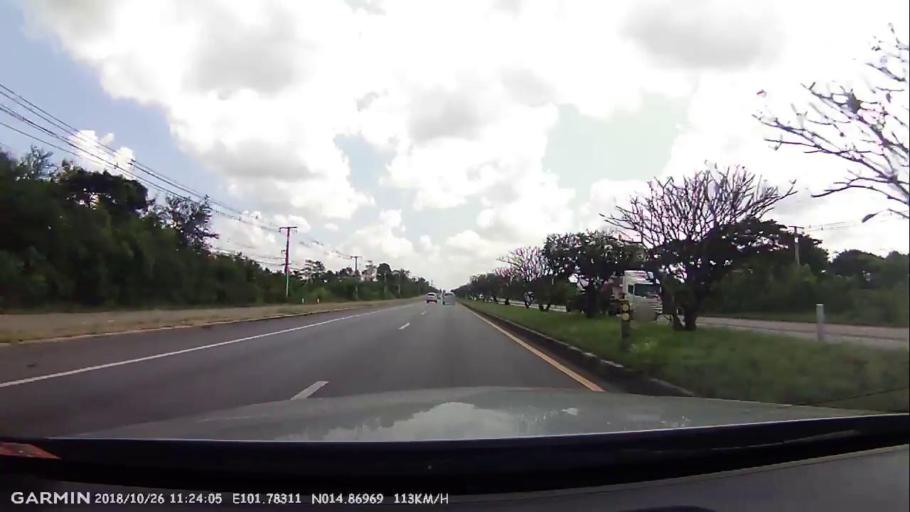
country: TH
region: Nakhon Ratchasima
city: Sung Noen
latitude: 14.8700
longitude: 101.7836
